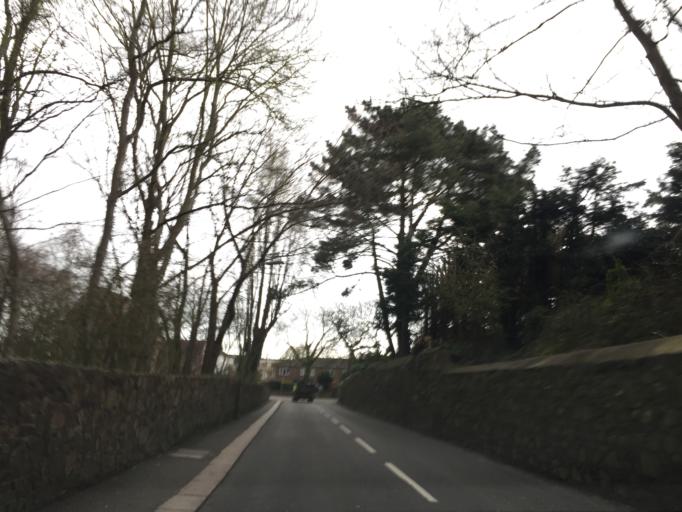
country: JE
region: St Helier
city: Saint Helier
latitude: 49.1943
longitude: -2.0919
